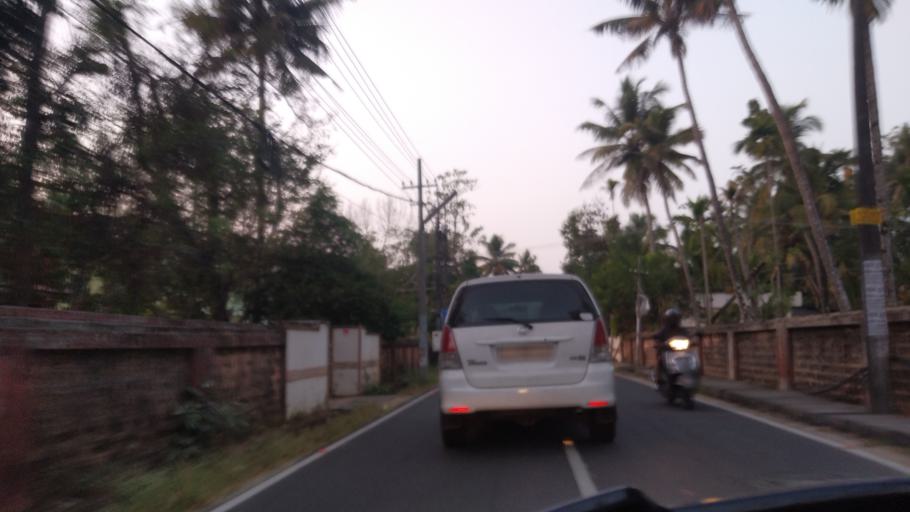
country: IN
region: Kerala
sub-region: Ernakulam
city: Elur
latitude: 10.1340
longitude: 76.2321
